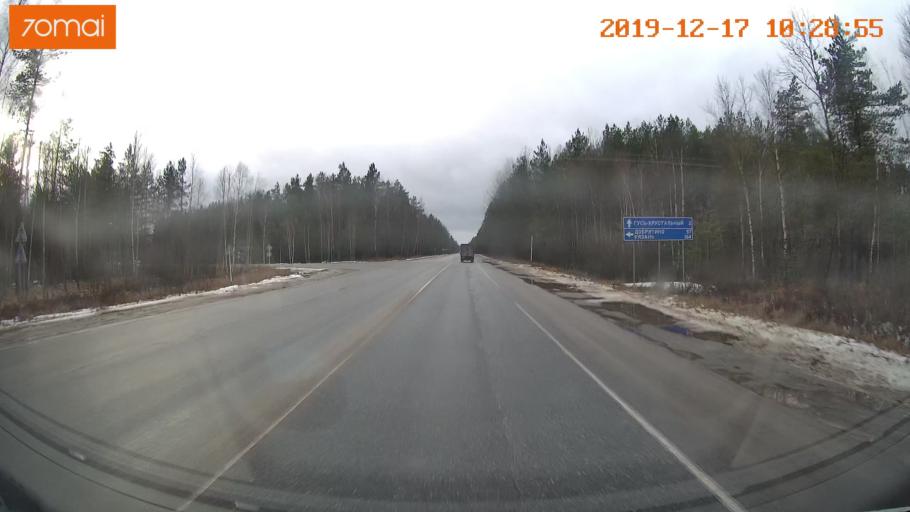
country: RU
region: Vladimir
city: Anopino
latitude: 55.6576
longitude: 40.7269
